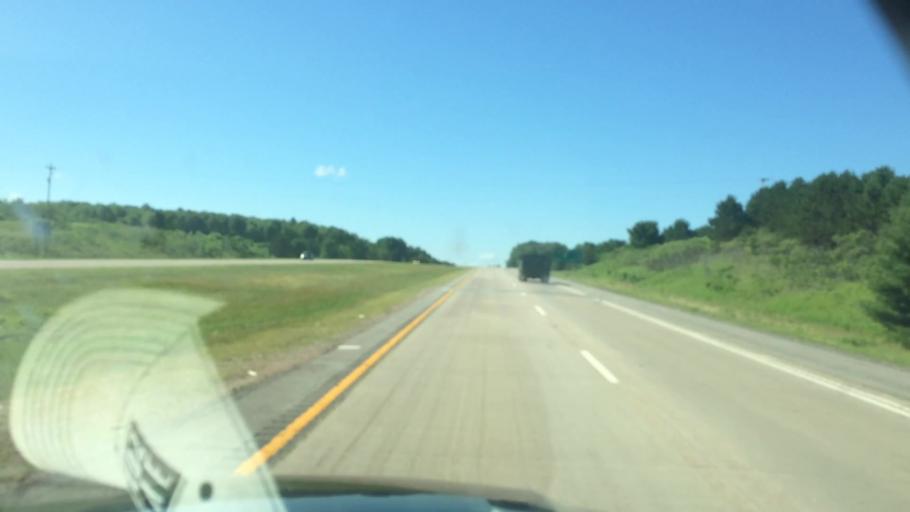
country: US
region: Wisconsin
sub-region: Marathon County
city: Mosinee
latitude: 44.6831
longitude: -89.6415
